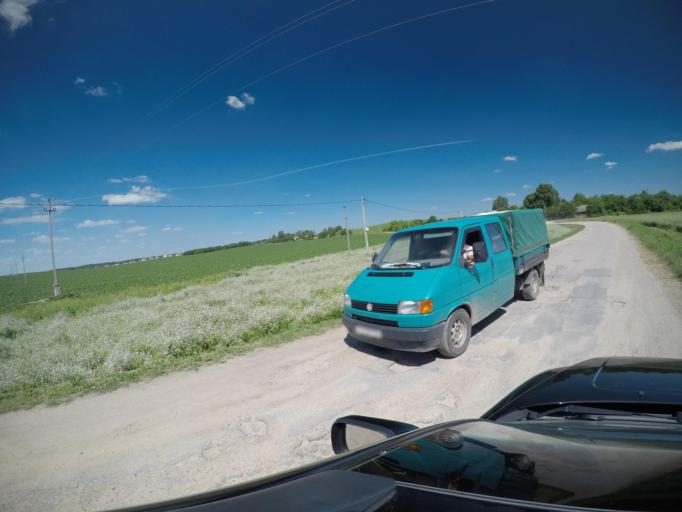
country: BY
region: Grodnenskaya
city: Hrodna
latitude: 53.7293
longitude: 23.8511
